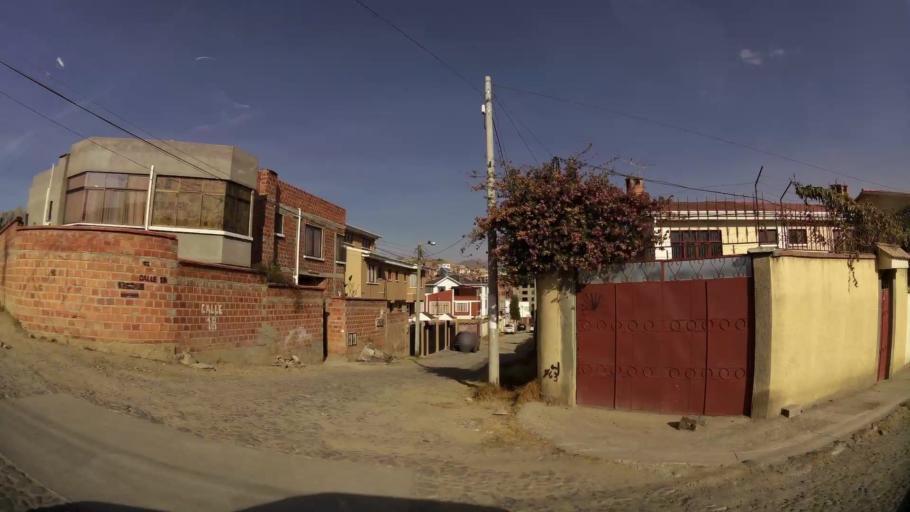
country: BO
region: La Paz
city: La Paz
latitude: -16.5084
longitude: -68.0836
